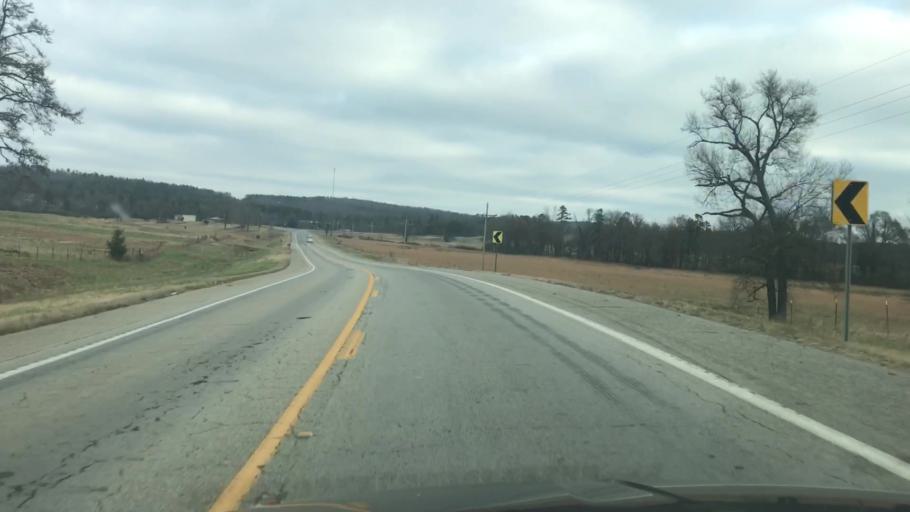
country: US
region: Arkansas
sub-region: Scott County
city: Waldron
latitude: 34.8014
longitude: -94.0417
